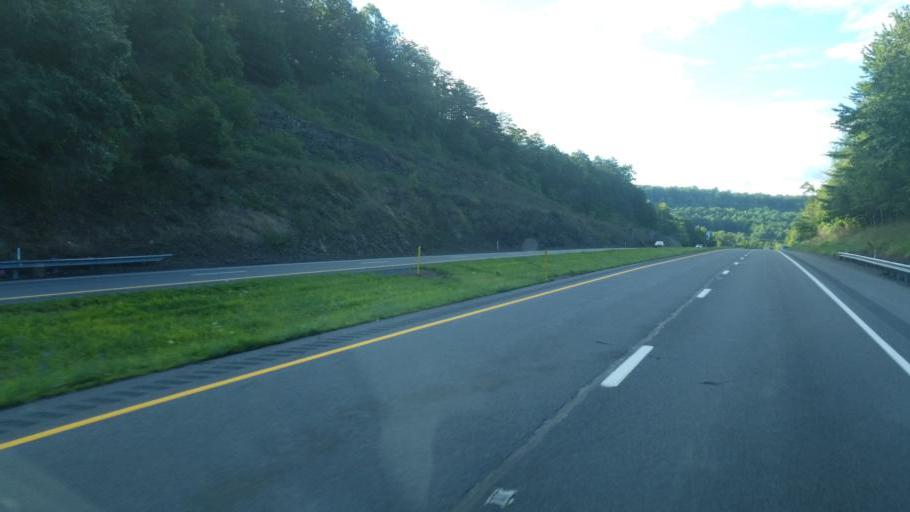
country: US
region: Maryland
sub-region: Washington County
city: Hancock
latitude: 39.7797
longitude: -78.2033
